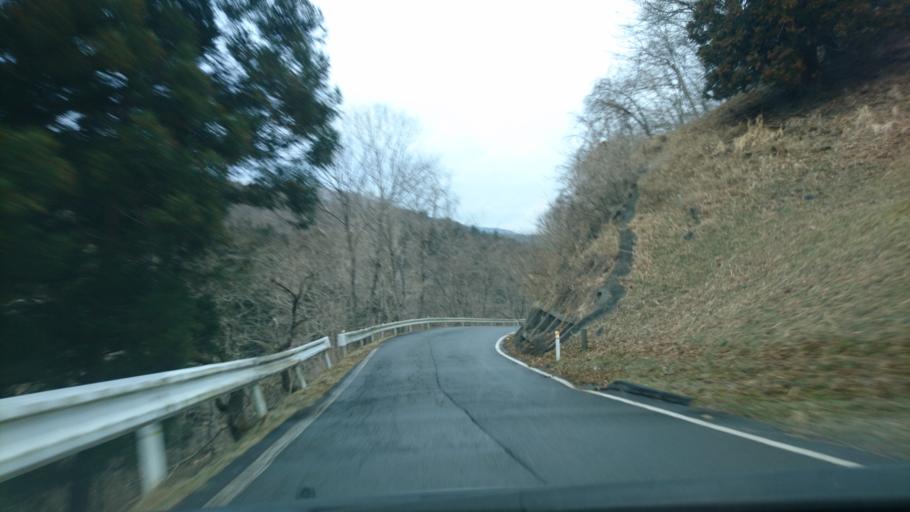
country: JP
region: Iwate
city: Ofunato
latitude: 39.0003
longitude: 141.5469
